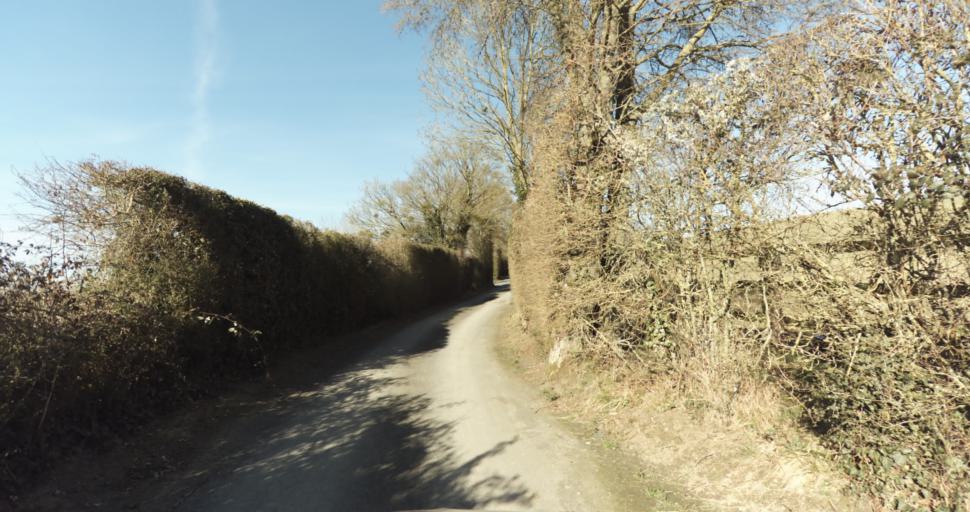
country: FR
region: Lower Normandy
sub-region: Departement du Calvados
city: Livarot
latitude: 49.0439
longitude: 0.0649
